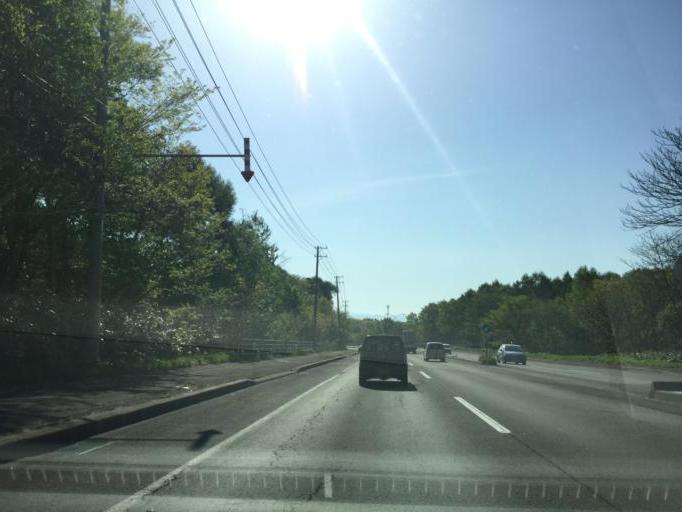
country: JP
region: Hokkaido
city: Kitahiroshima
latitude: 42.9990
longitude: 141.5393
